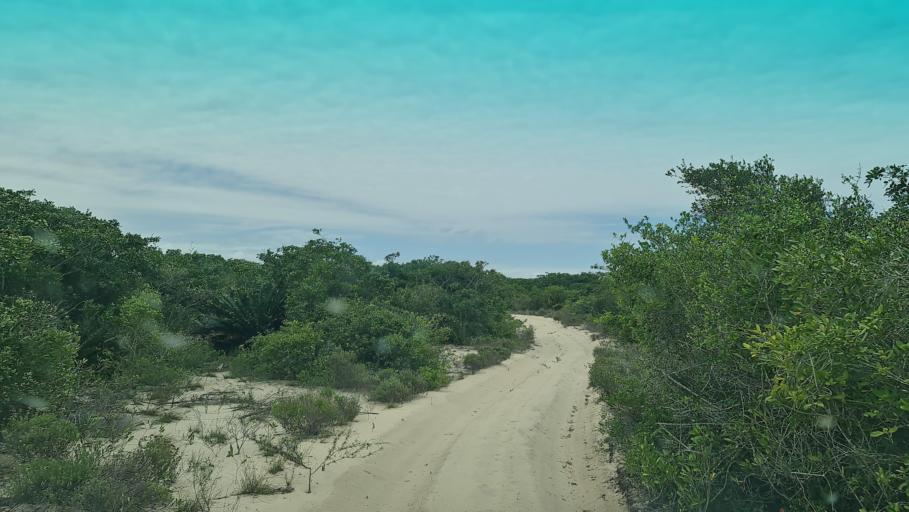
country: MZ
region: Maputo
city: Manhica
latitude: -25.6390
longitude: 32.7829
